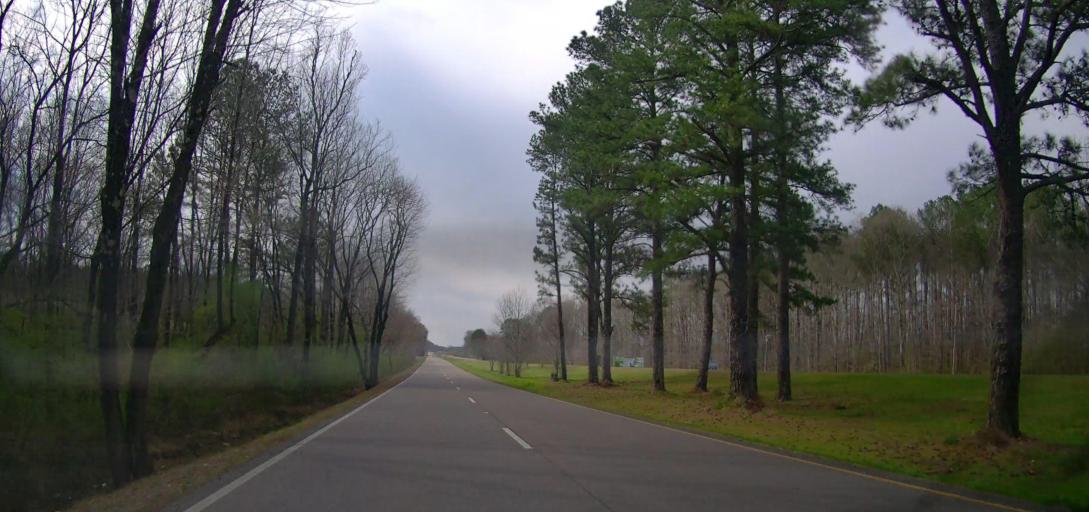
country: US
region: Alabama
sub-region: Walker County
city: Carbon Hill
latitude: 33.8788
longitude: -87.5019
